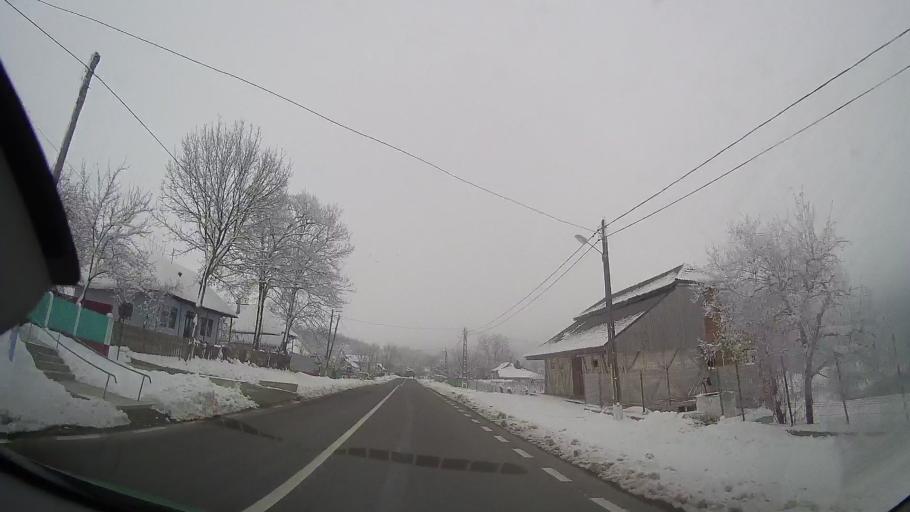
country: RO
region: Neamt
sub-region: Comuna Poenari
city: Poienari
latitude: 46.8852
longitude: 27.1314
